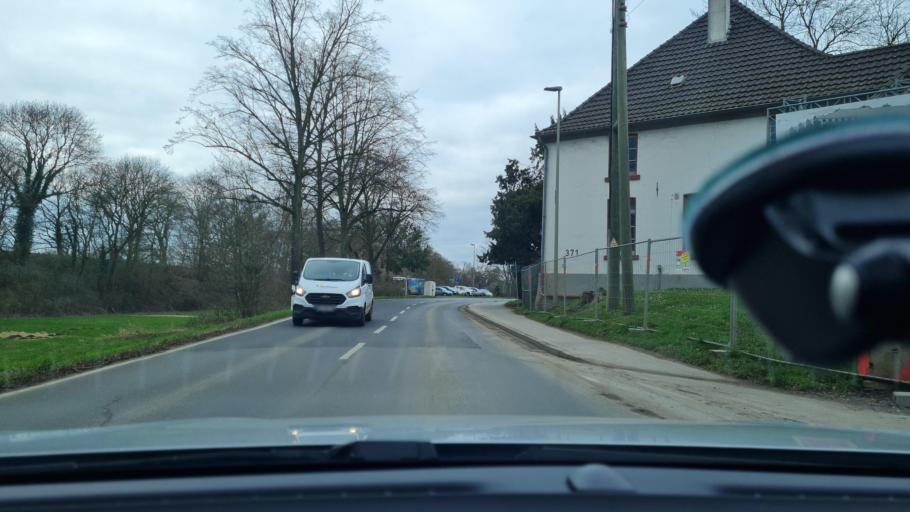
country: DE
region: North Rhine-Westphalia
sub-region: Regierungsbezirk Dusseldorf
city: Voerde
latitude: 51.5947
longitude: 6.6685
